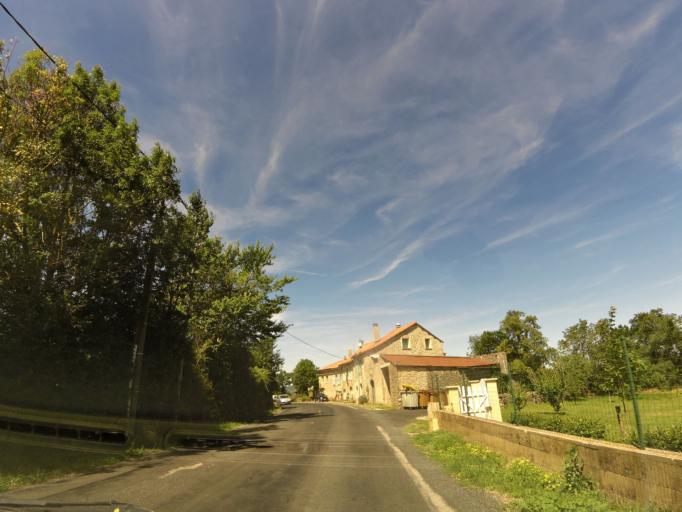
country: FR
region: Midi-Pyrenees
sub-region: Departement de l'Aveyron
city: La Cavalerie
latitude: 43.9503
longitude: 3.2662
